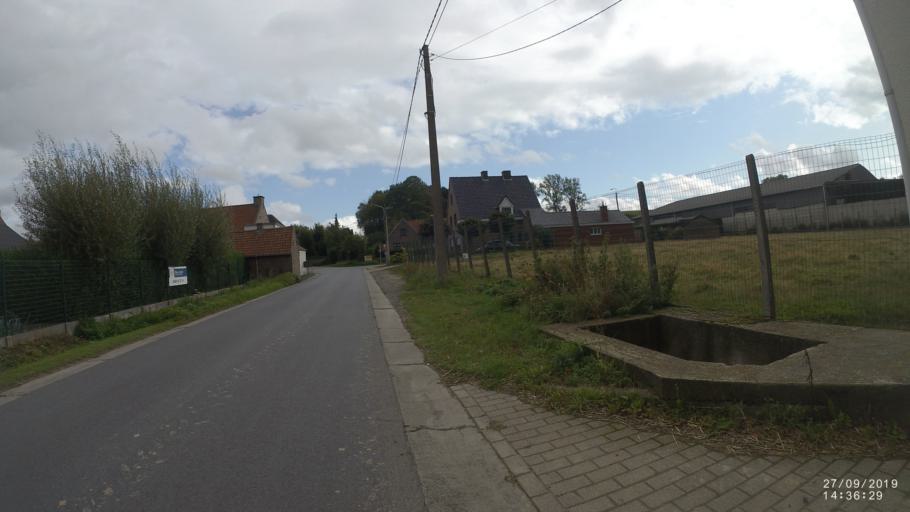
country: BE
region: Flanders
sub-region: Provincie Oost-Vlaanderen
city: Zingem
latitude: 50.8666
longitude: 3.6710
